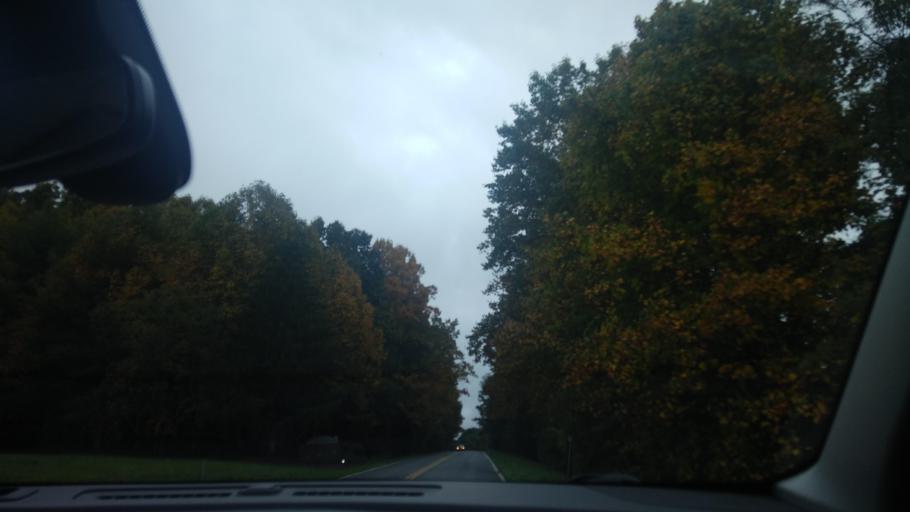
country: US
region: Virginia
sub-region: City of Galax
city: Galax
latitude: 36.6325
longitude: -80.9194
